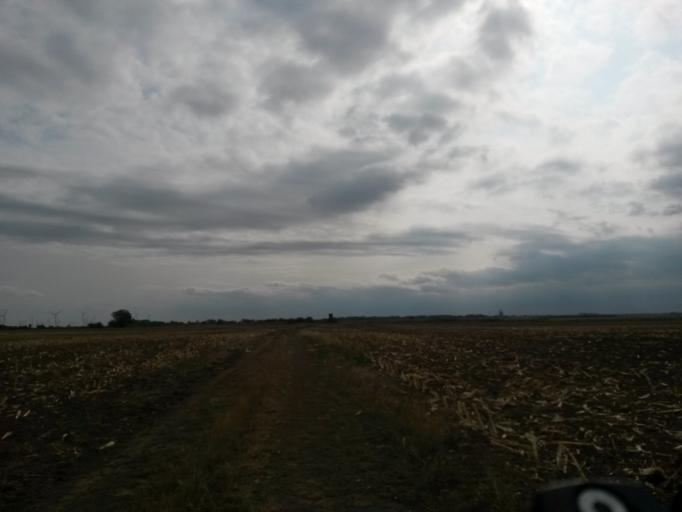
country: DE
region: Saxony-Anhalt
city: Tangermunde
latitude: 52.5173
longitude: 11.9725
